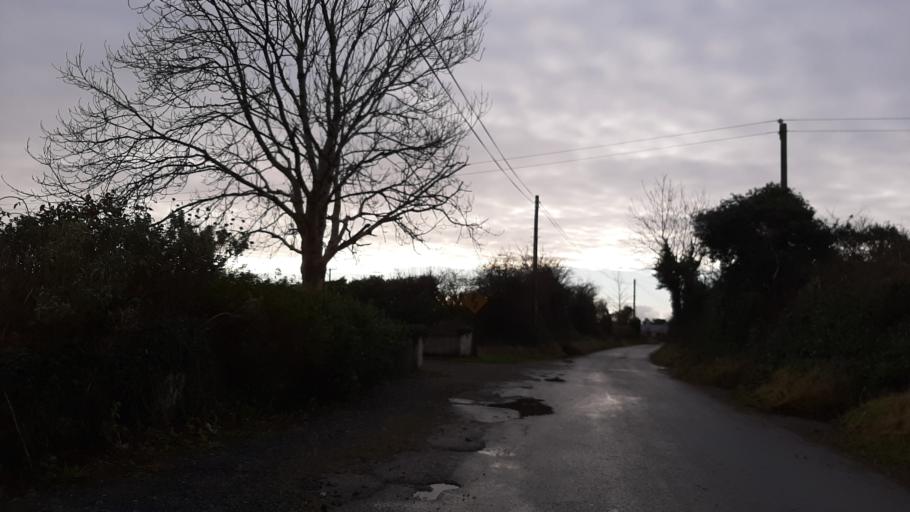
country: IE
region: Connaught
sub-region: County Galway
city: Gaillimh
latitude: 53.3085
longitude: -9.0682
